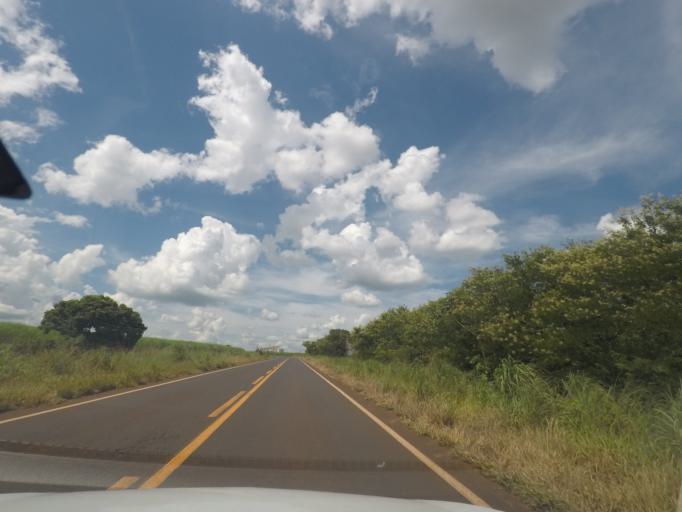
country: BR
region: Minas Gerais
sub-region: Conceicao Das Alagoas
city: Conceicao das Alagoas
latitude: -19.8134
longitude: -48.5855
